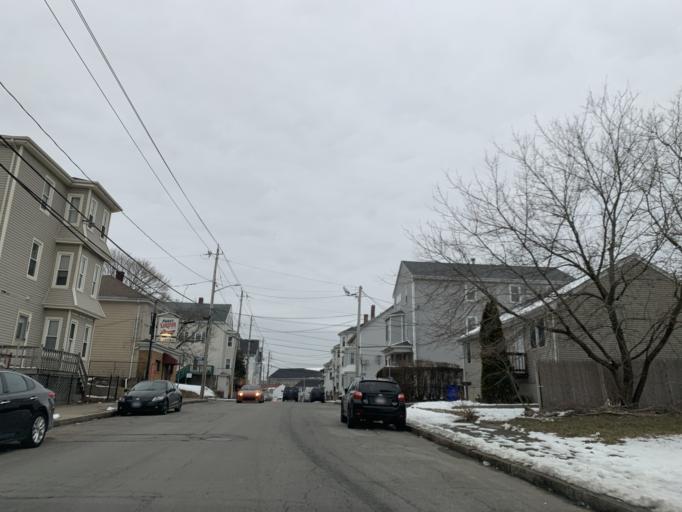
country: US
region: Massachusetts
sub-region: Bristol County
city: Fall River
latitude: 41.6887
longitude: -71.1478
